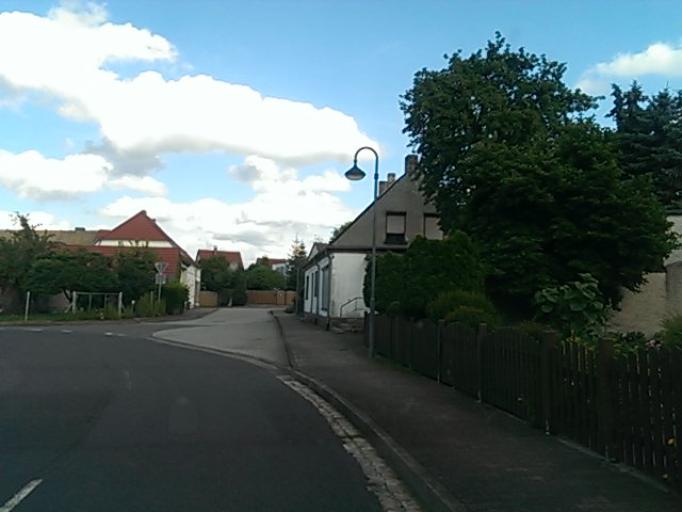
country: DE
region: Saxony-Anhalt
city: Coswig
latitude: 51.9571
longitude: 12.4904
